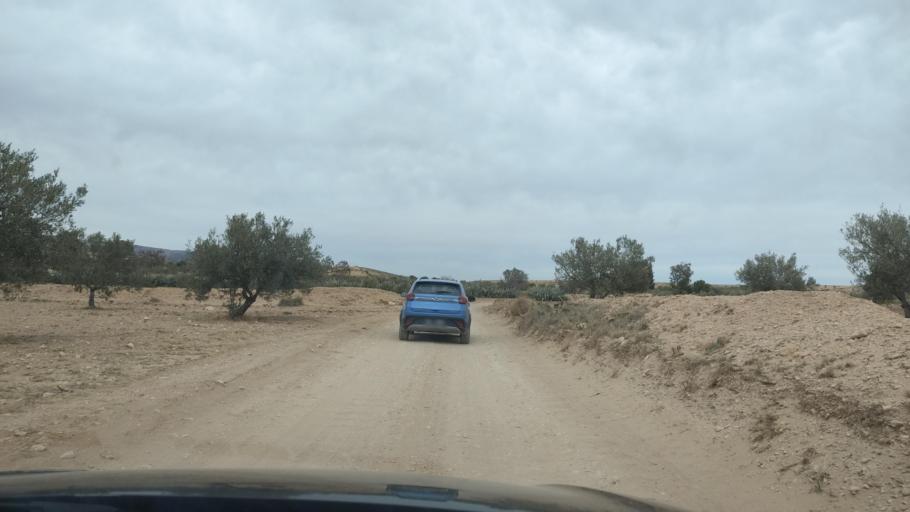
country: TN
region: Al Qasrayn
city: Kasserine
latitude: 35.2554
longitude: 8.9217
